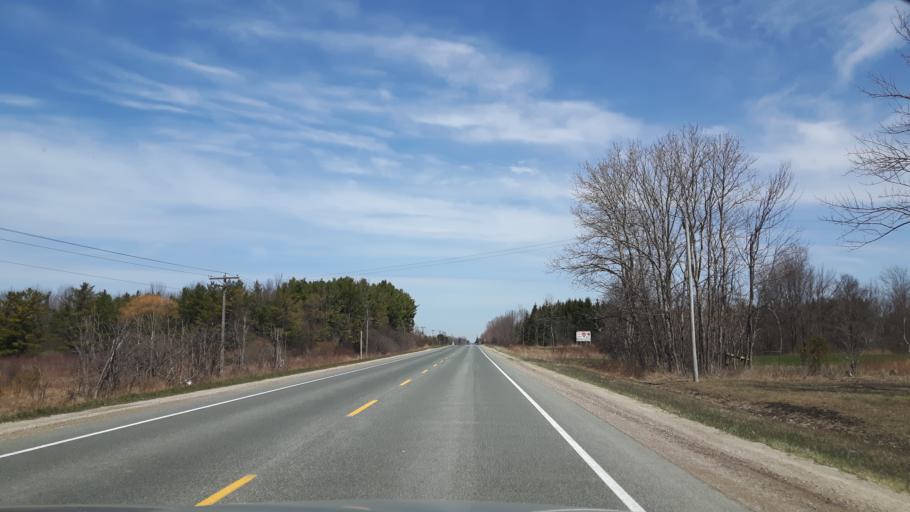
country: CA
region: Ontario
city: Goderich
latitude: 43.6812
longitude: -81.7056
